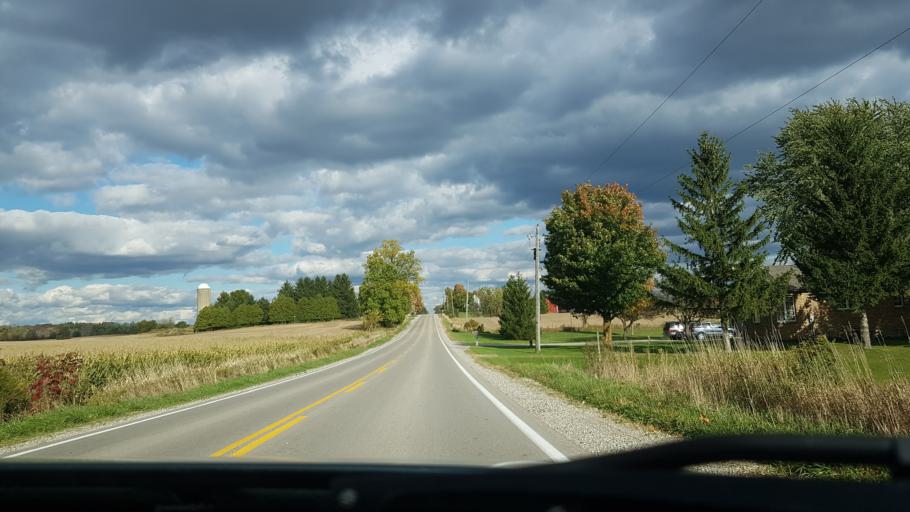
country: CA
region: Ontario
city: Delaware
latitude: 43.0173
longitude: -81.3606
